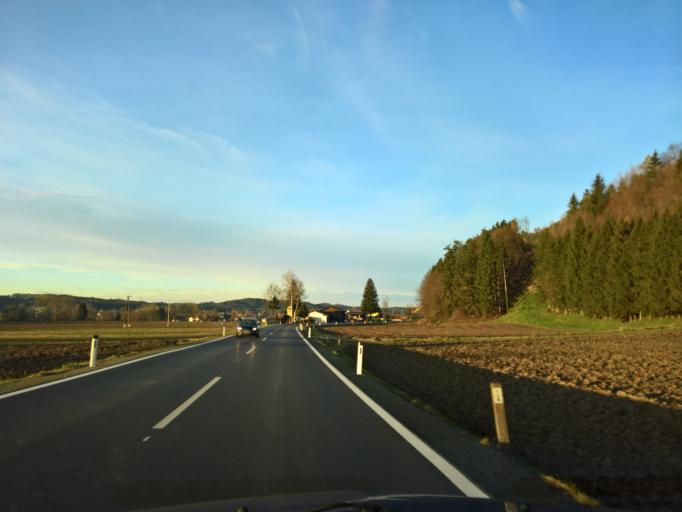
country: AT
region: Styria
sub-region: Politischer Bezirk Leibnitz
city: Arnfels
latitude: 46.6895
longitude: 15.3955
